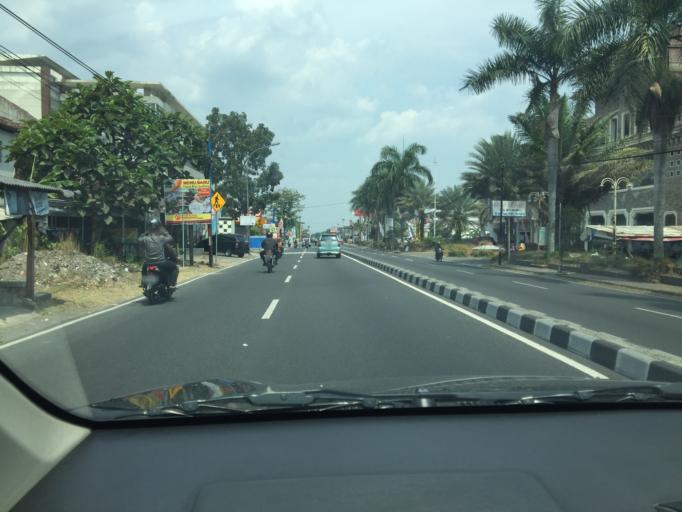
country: ID
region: Daerah Istimewa Yogyakarta
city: Sleman
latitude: -7.6859
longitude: 110.3410
